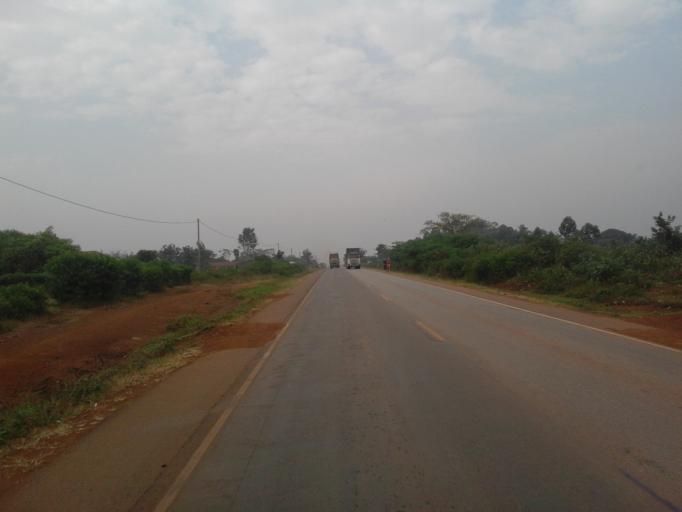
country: UG
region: Eastern Region
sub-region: Busia District
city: Busia
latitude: 0.5790
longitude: 34.0454
